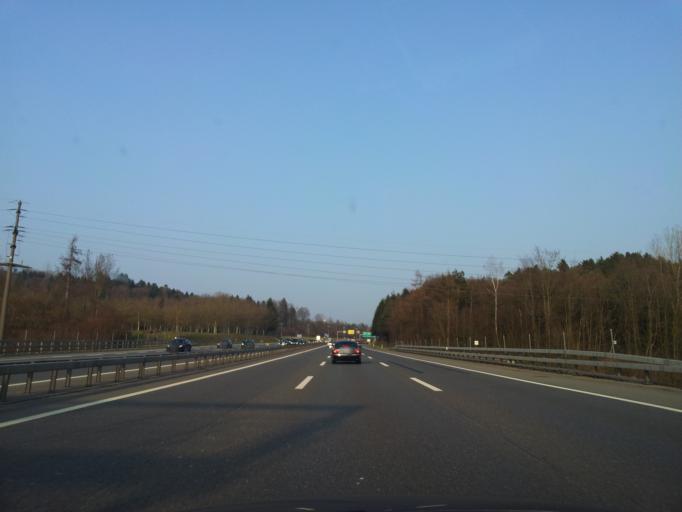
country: CH
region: Aargau
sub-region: Bezirk Baden
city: Birmenstorf
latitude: 47.4539
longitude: 8.2686
